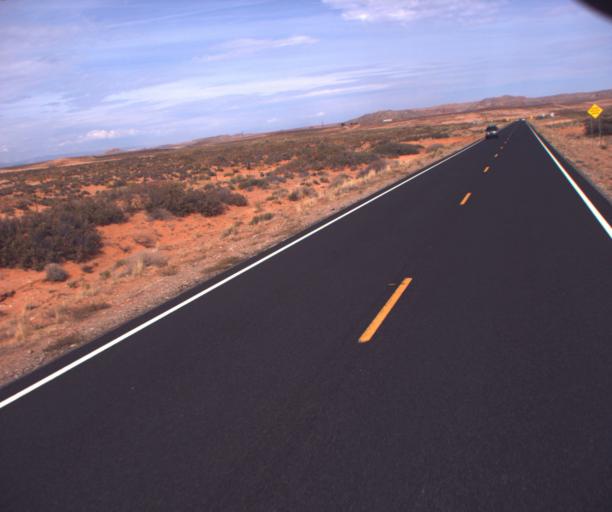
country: US
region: Arizona
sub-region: Apache County
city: Many Farms
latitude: 36.9191
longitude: -109.6190
